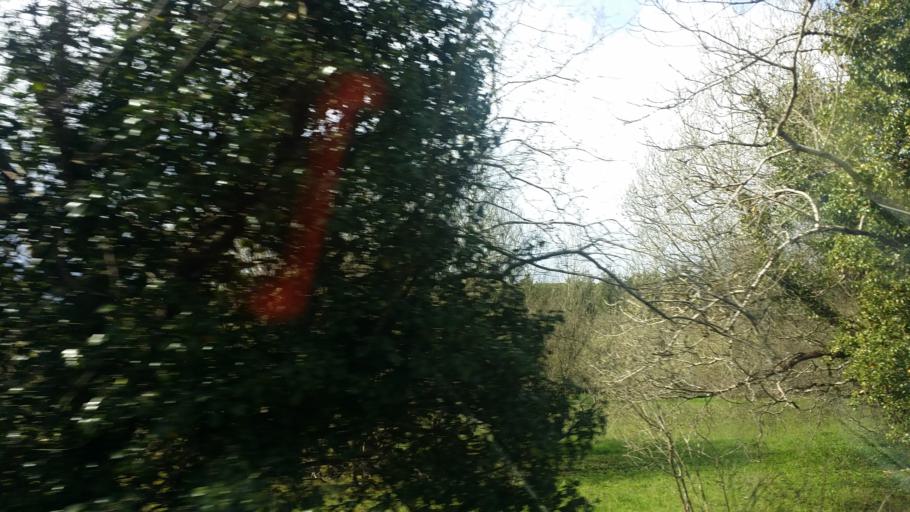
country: GB
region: Northern Ireland
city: Irvinestown
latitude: 54.4418
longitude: -7.7937
